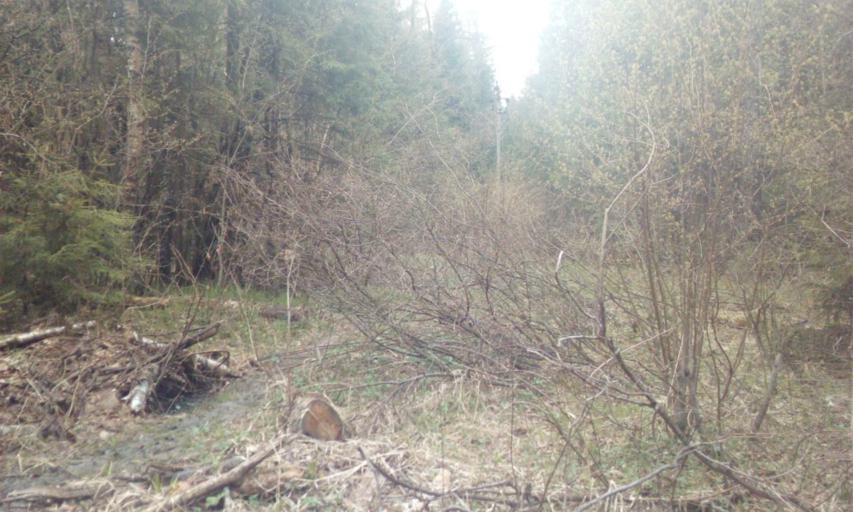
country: RU
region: Moskovskaya
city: Annino
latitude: 55.5410
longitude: 37.2255
